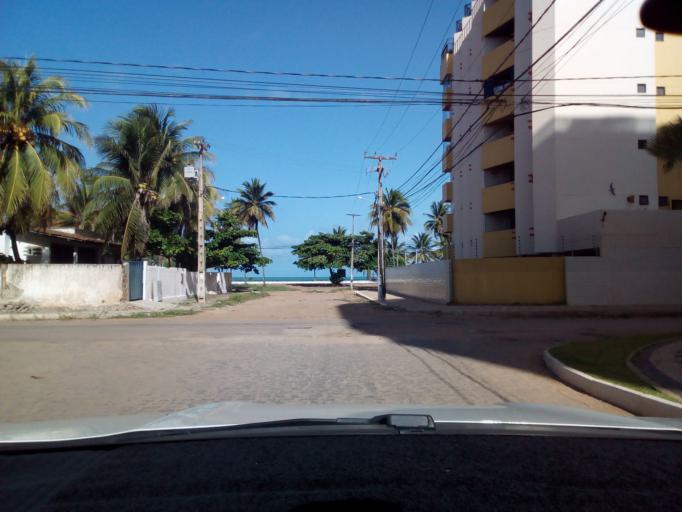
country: BR
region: Paraiba
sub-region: Cabedelo
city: Cabedelo
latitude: -7.0430
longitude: -34.8418
